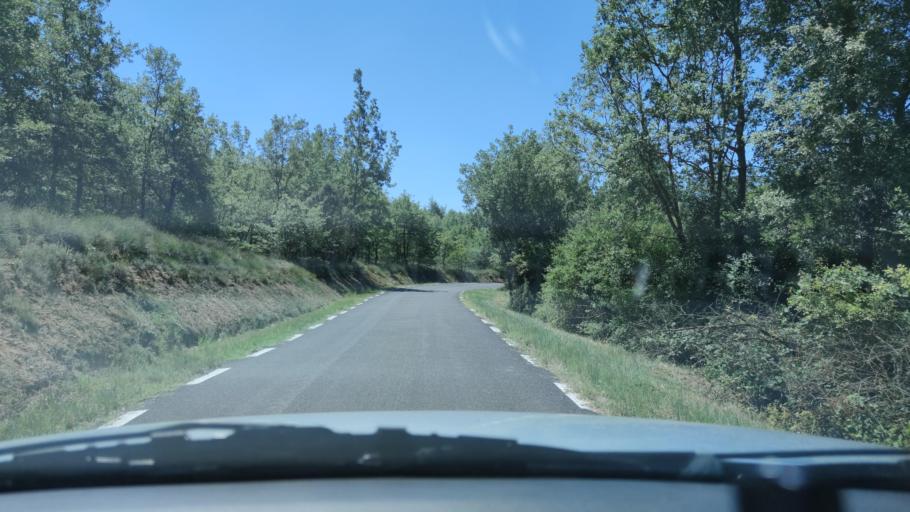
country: ES
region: Catalonia
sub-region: Provincia de Lleida
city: Tora de Riubregos
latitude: 41.8937
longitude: 1.4407
